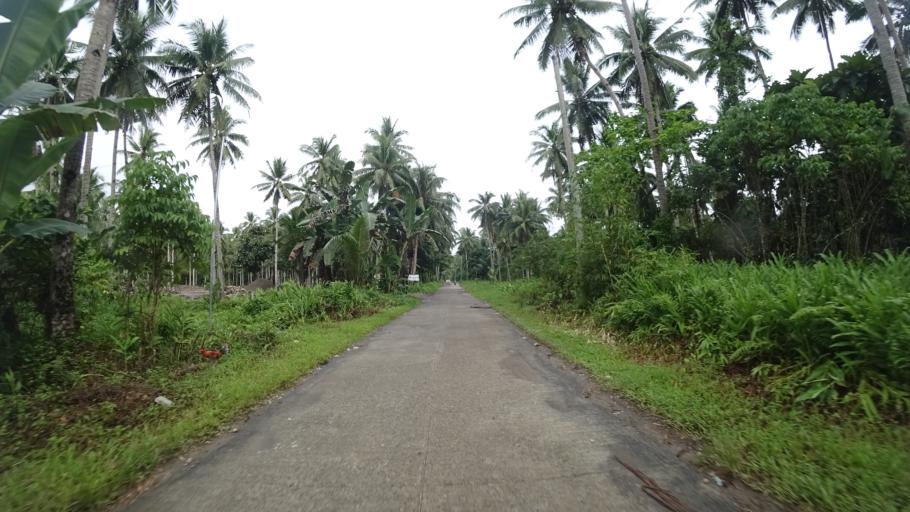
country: PH
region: Eastern Visayas
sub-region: Province of Leyte
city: Bugho
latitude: 10.8255
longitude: 124.9221
